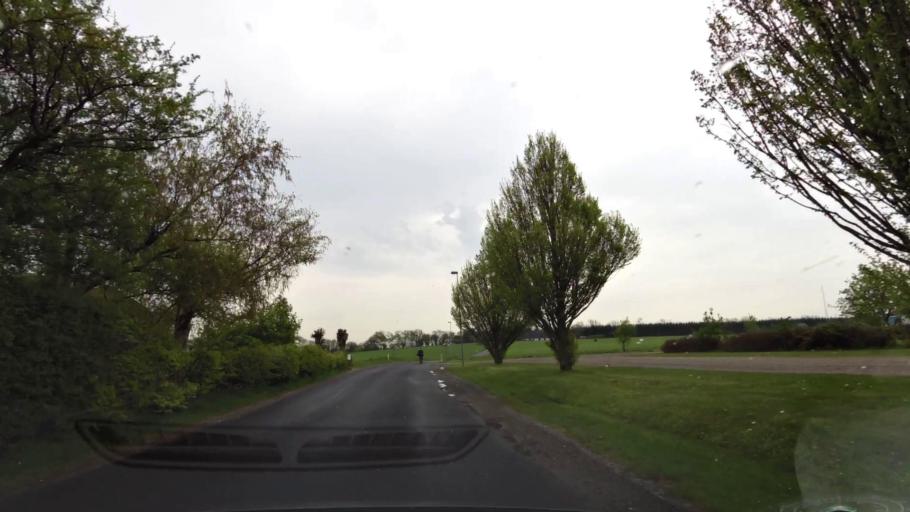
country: DK
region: South Denmark
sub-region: Svendborg Kommune
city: Thuro By
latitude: 55.1484
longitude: 10.7112
